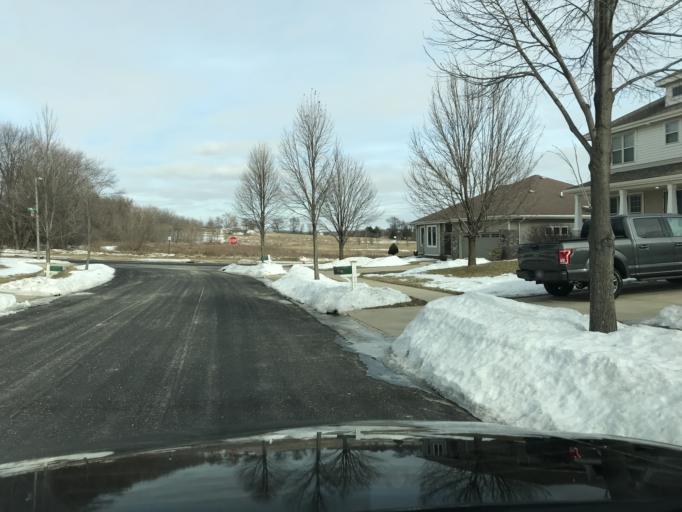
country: US
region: Wisconsin
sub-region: Dane County
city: Cottage Grove
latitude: 43.0880
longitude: -89.2635
